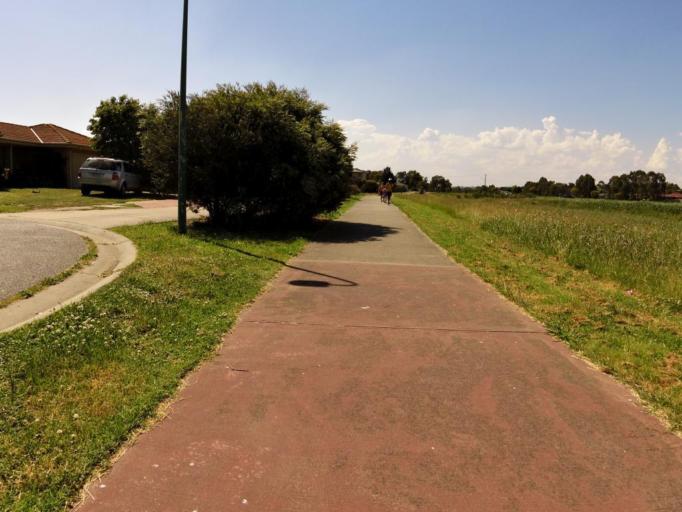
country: AU
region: Victoria
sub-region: Casey
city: Narre Warren South
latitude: -38.0468
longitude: 145.2774
